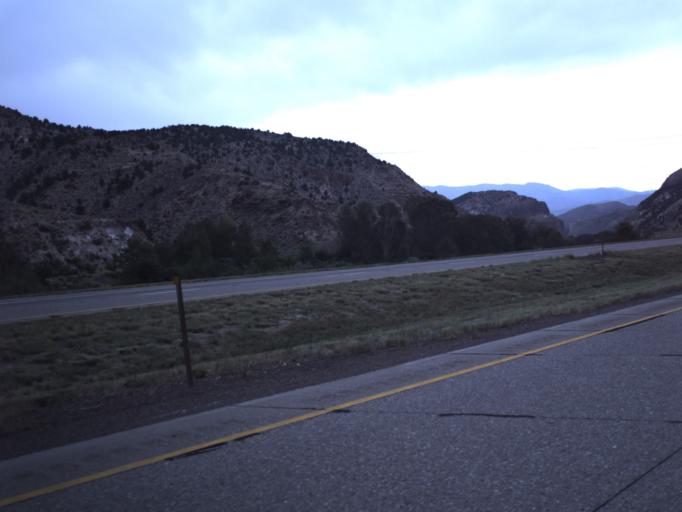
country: US
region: Utah
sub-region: Sevier County
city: Monroe
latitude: 38.5782
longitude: -112.3244
